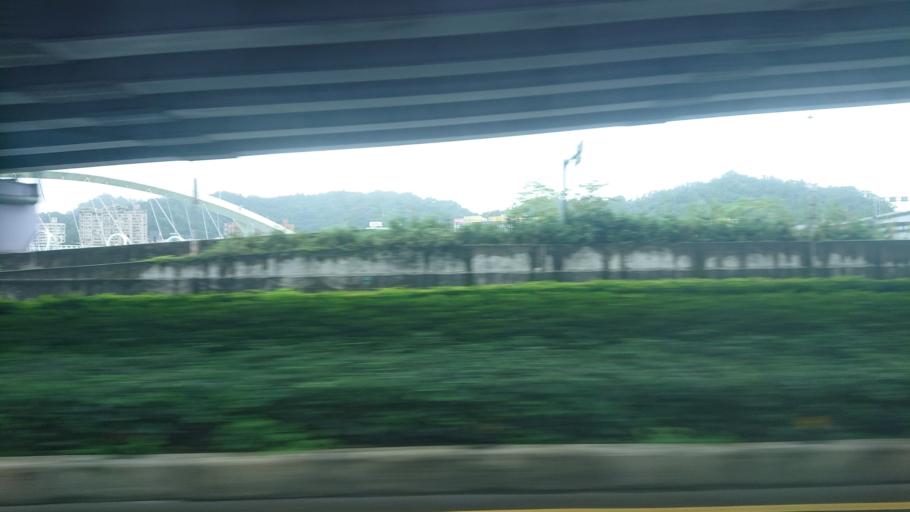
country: TW
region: Taipei
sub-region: Taipei
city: Banqiao
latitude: 24.9795
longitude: 121.5233
